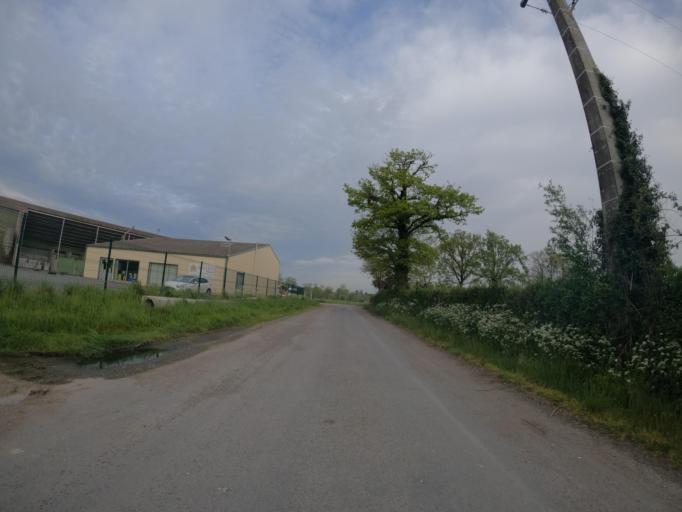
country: FR
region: Poitou-Charentes
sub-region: Departement des Deux-Sevres
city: La Chapelle-Saint-Laurent
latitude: 46.6995
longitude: -0.4911
